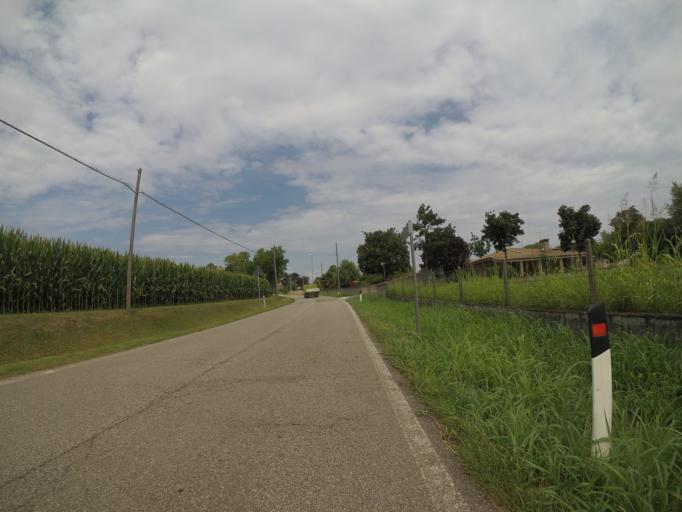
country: IT
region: Friuli Venezia Giulia
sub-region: Provincia di Udine
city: Basiliano-Vissandone
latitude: 45.9786
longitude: 13.0971
